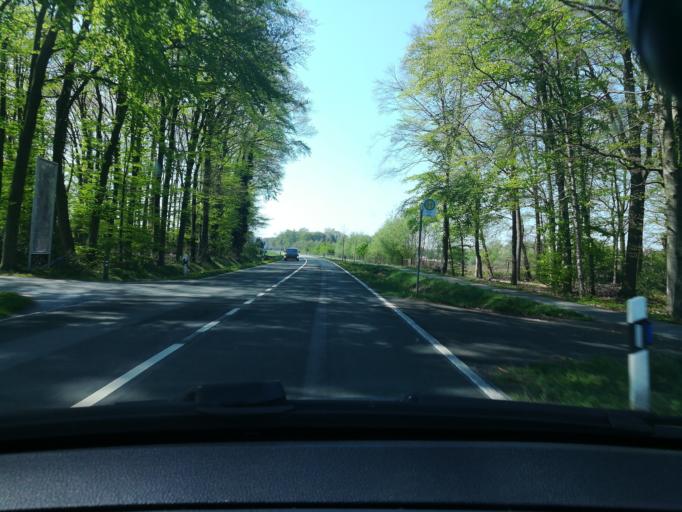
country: DE
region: North Rhine-Westphalia
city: Versmold
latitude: 52.0086
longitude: 8.1734
